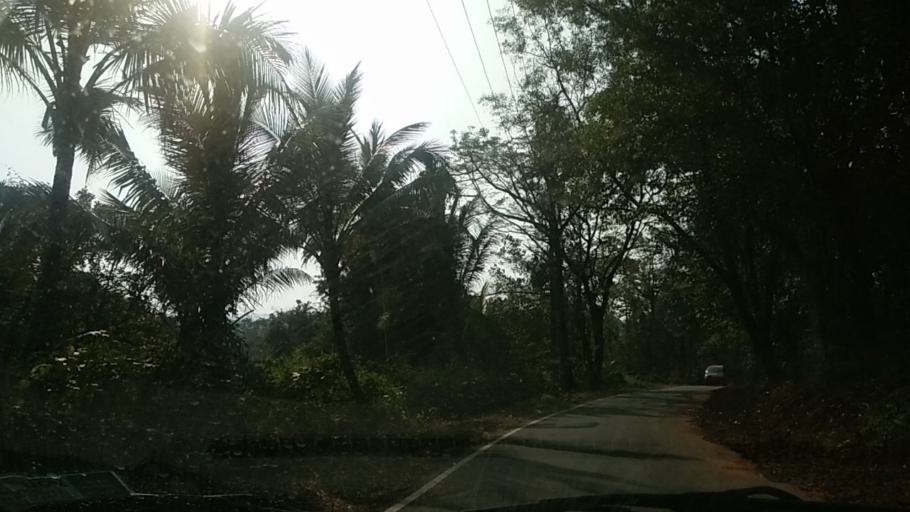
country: IN
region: Goa
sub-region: South Goa
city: Sanguem
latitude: 15.1842
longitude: 74.2276
